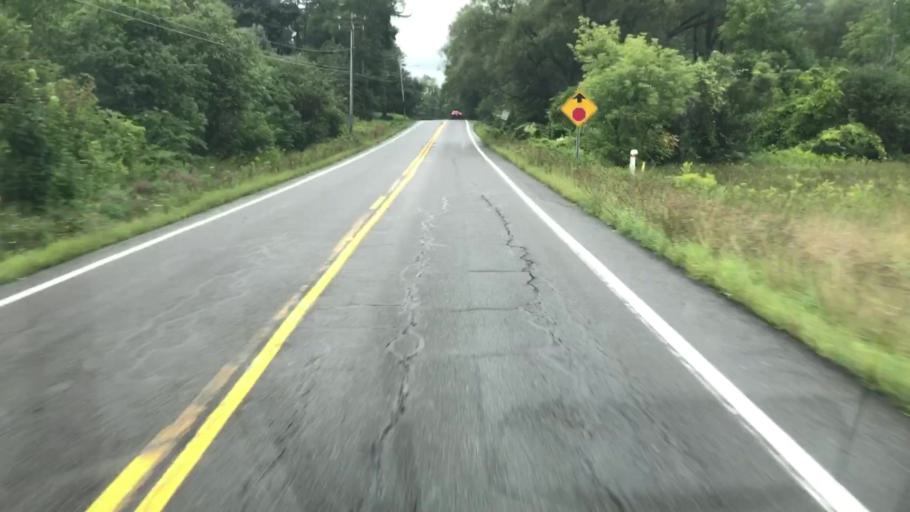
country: US
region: New York
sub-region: Onondaga County
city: Skaneateles
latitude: 42.9655
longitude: -76.4336
